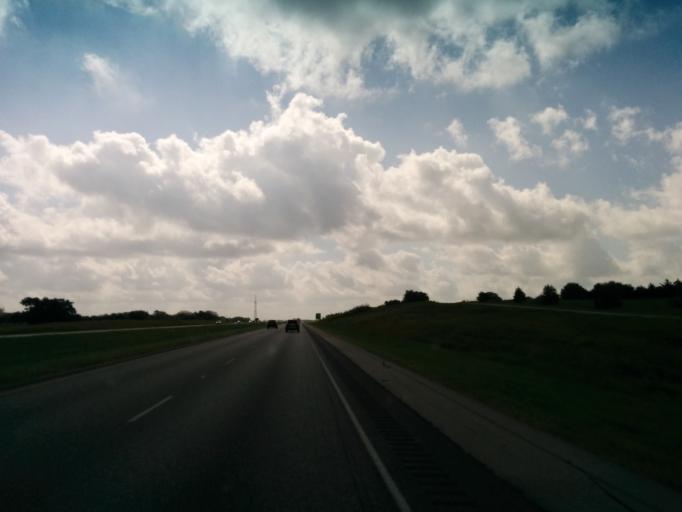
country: US
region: Texas
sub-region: Fayette County
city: Flatonia
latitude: 29.6945
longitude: -97.0257
